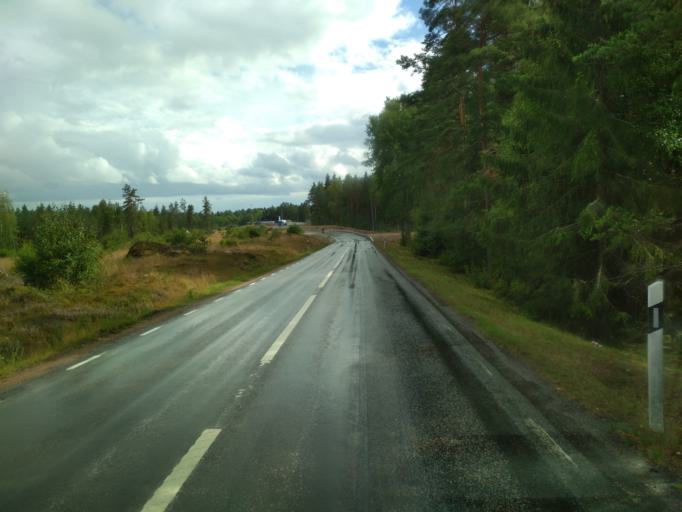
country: SE
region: Vaestmanland
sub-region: Hallstahammars Kommun
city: Hallstahammar
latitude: 59.6355
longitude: 16.1979
